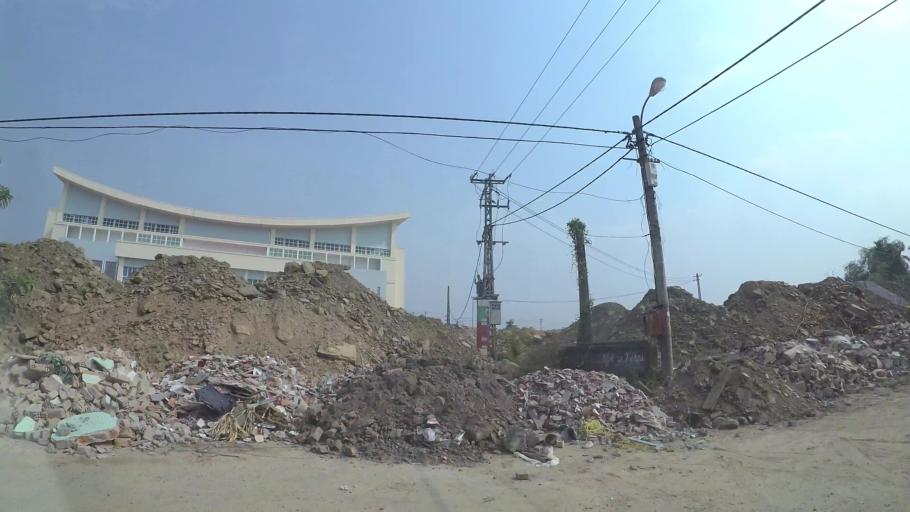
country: VN
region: Da Nang
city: Cam Le
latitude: 15.9969
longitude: 108.2186
